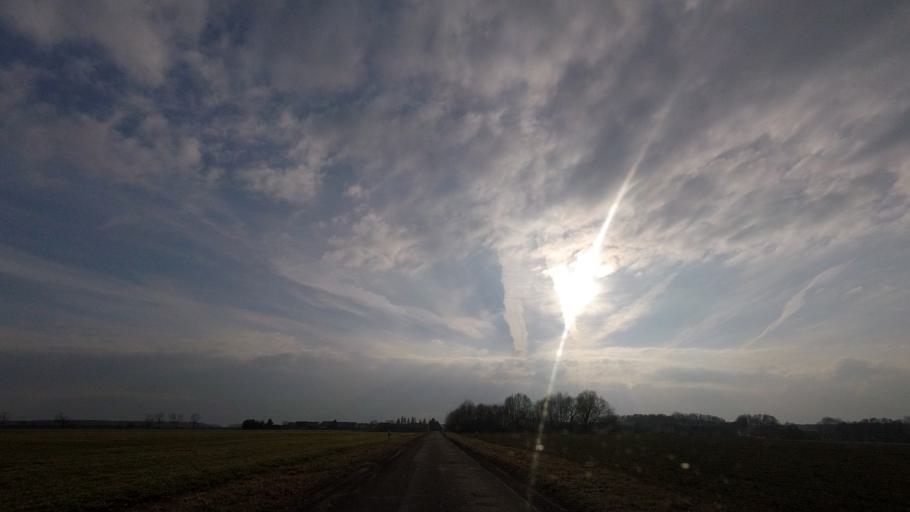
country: DE
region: Brandenburg
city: Belzig
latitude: 52.1529
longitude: 12.6608
